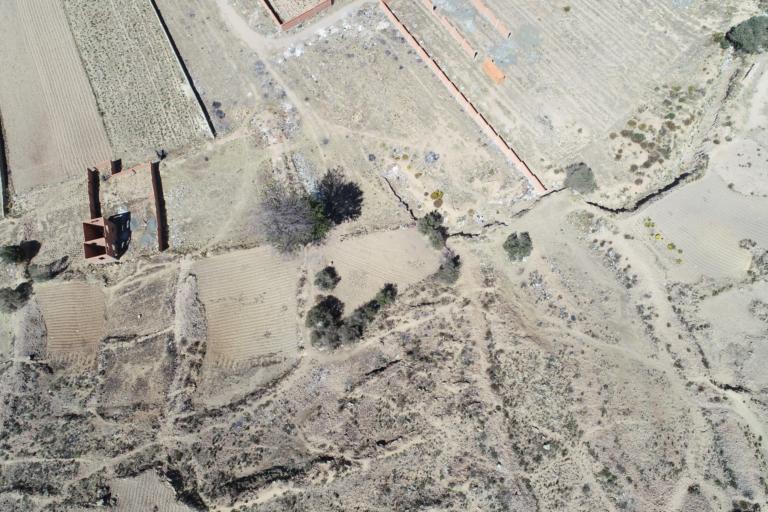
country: BO
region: La Paz
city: Achacachi
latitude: -16.0460
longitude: -68.6784
